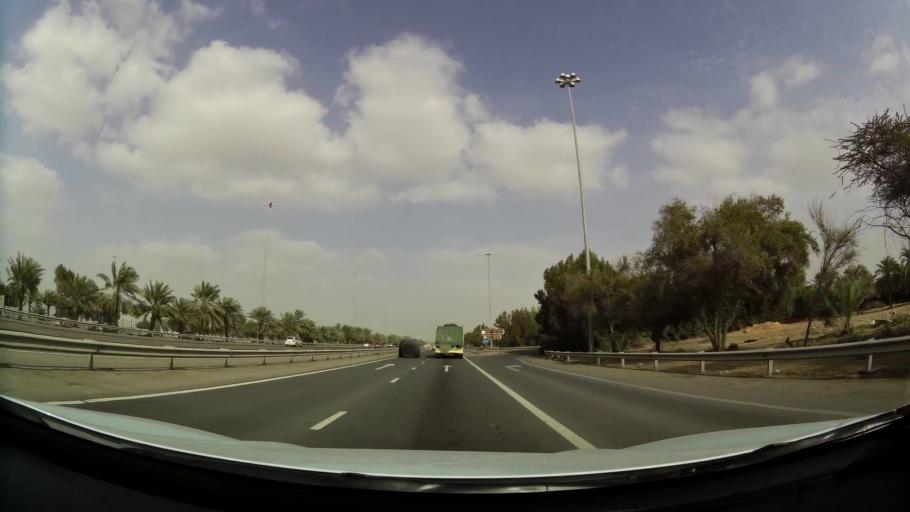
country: AE
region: Abu Dhabi
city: Abu Dhabi
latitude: 24.4235
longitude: 54.5251
